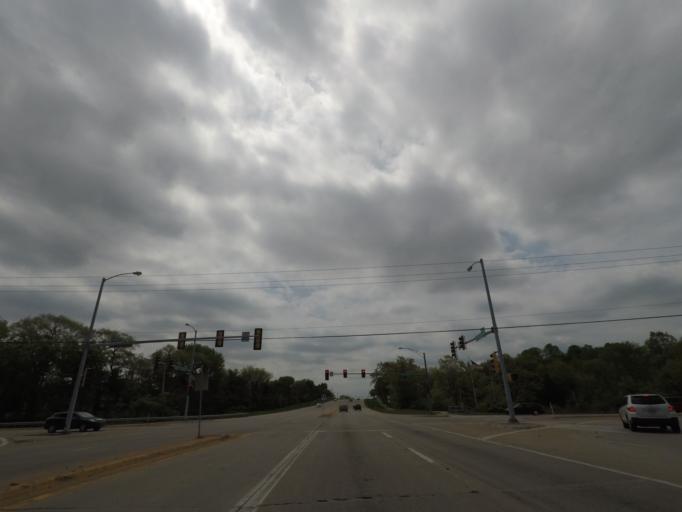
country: US
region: Illinois
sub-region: Winnebago County
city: Cherry Valley
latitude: 42.2828
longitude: -88.9799
